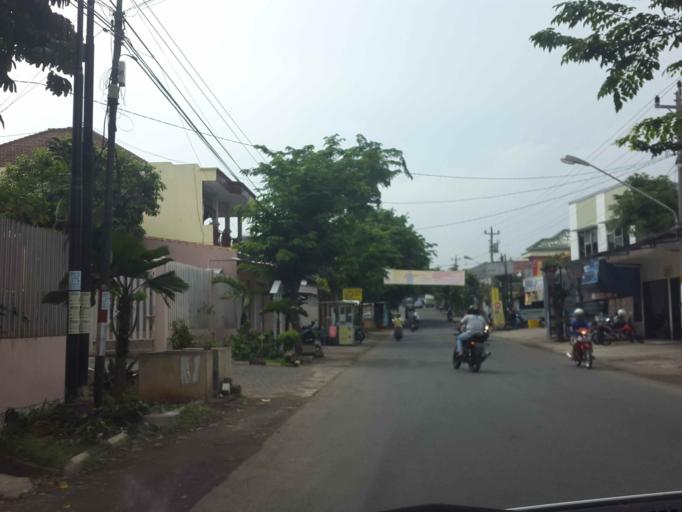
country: ID
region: Central Java
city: Semarang
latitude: -7.0600
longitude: 110.4408
